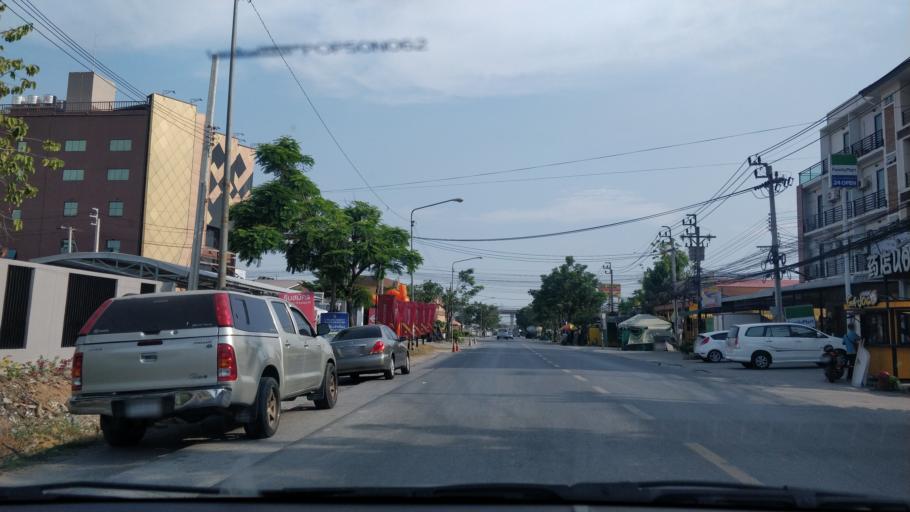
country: TH
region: Bangkok
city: Saphan Sung
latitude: 13.7359
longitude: 100.7161
